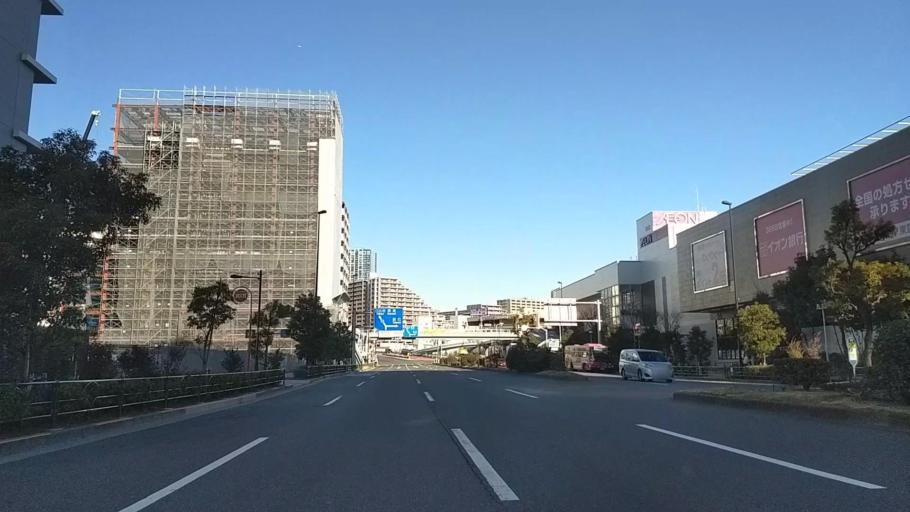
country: JP
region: Tokyo
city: Urayasu
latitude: 35.6480
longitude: 139.8015
